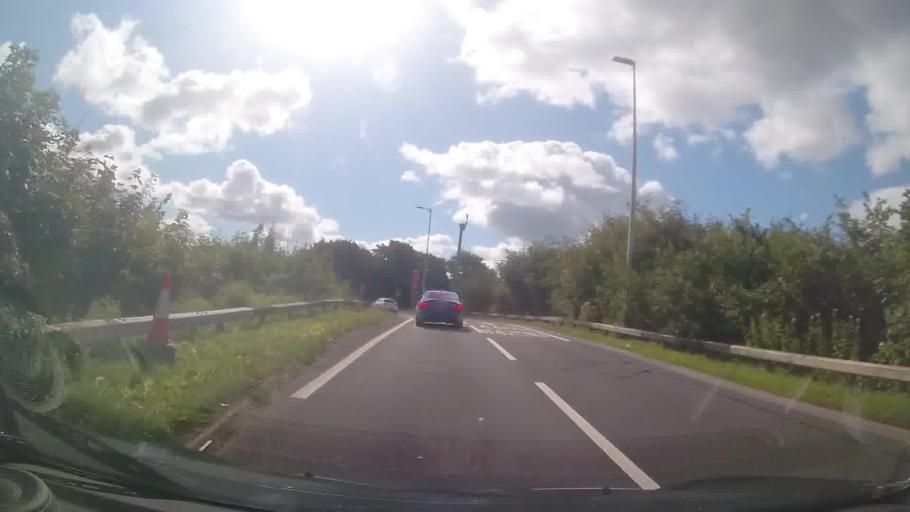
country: GB
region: Wales
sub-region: Neath Port Talbot
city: Briton Ferry
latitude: 51.6501
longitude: -3.8499
